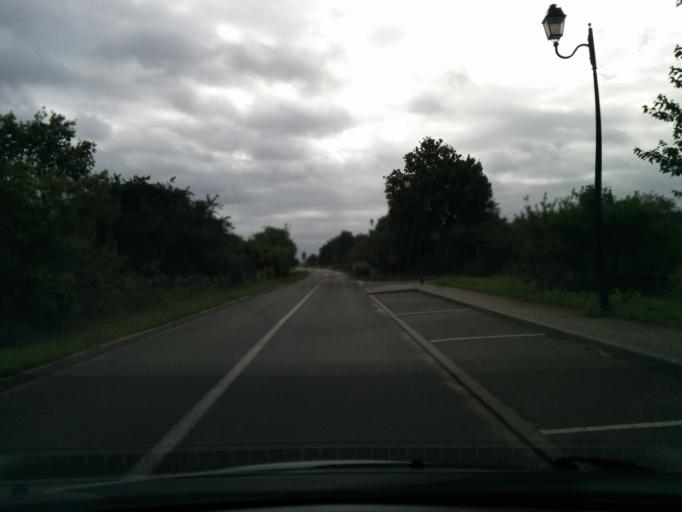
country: FR
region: Ile-de-France
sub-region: Departement des Yvelines
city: Rosny-sur-Seine
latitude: 49.0116
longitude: 1.6409
